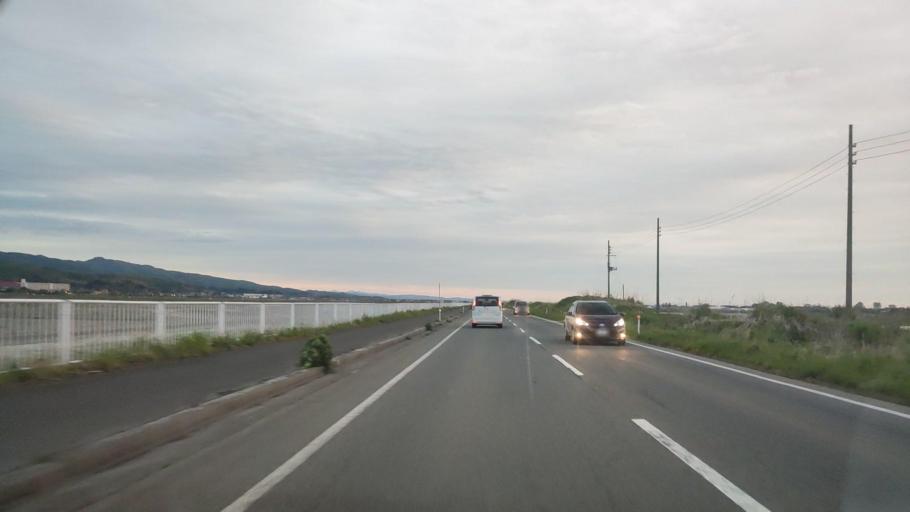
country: JP
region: Niigata
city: Niitsu-honcho
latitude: 37.7683
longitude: 139.1007
